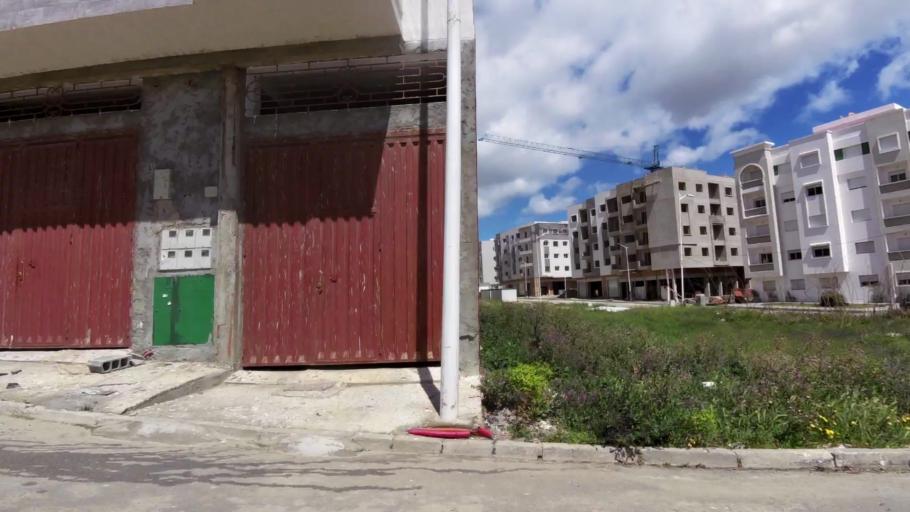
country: MA
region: Tanger-Tetouan
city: Tetouan
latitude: 35.5807
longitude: -5.3411
